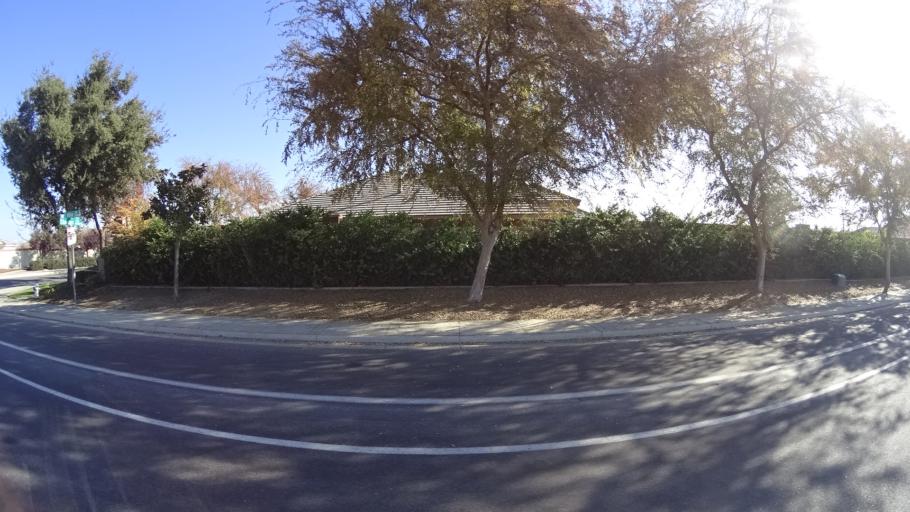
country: US
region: California
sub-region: Kern County
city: Rosedale
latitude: 35.3321
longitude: -119.1455
